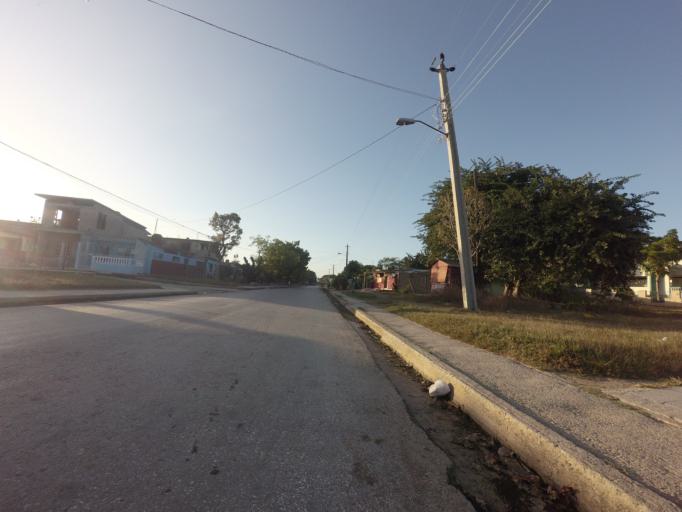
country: CU
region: Ciego de Avila
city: Ciego de Avila
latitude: 21.8299
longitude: -78.7535
